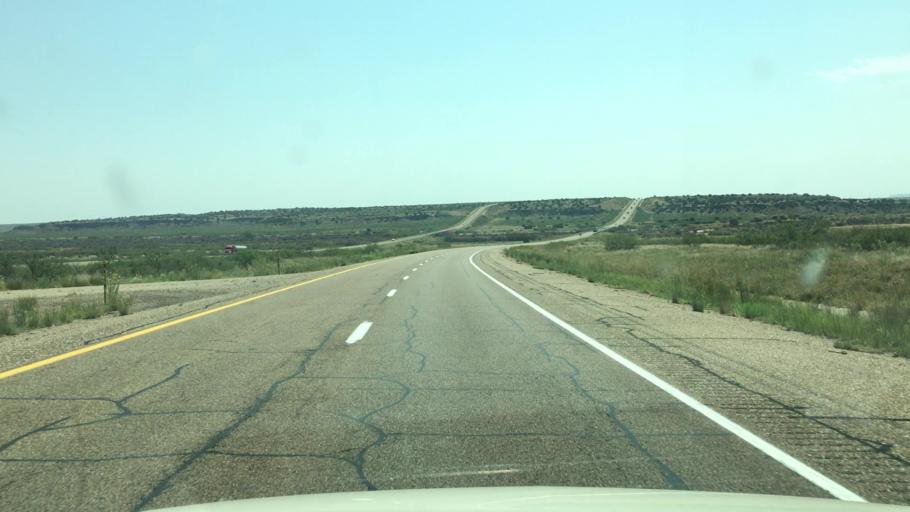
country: US
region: New Mexico
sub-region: Quay County
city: Logan
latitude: 35.1720
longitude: -103.4838
